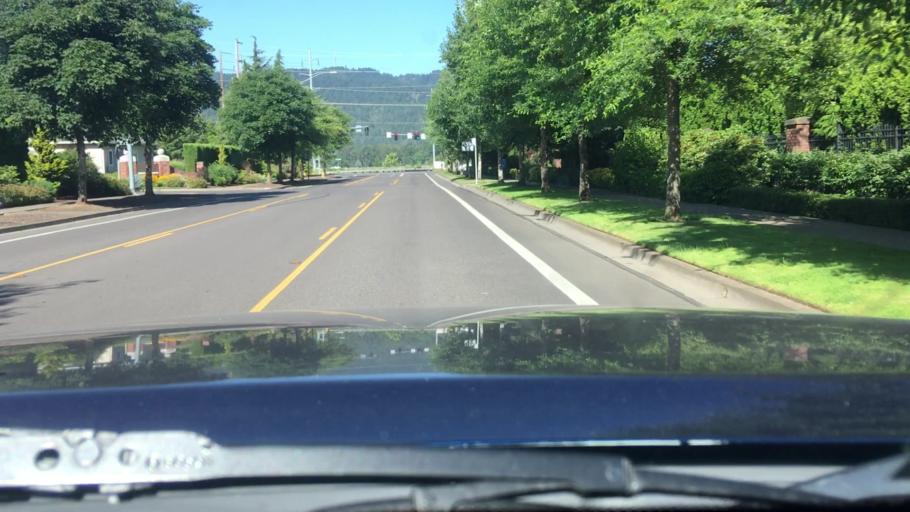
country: US
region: Oregon
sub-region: Lane County
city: Coburg
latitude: 44.0941
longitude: -123.0531
